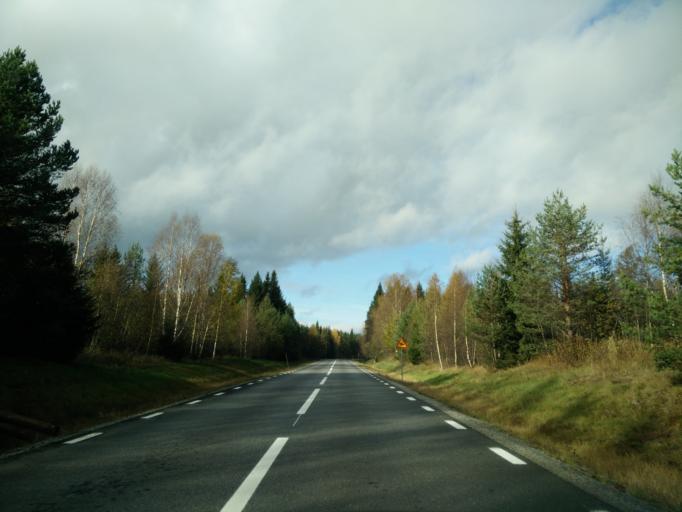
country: SE
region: Jaemtland
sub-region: Braecke Kommun
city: Braecke
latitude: 62.4180
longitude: 15.0095
